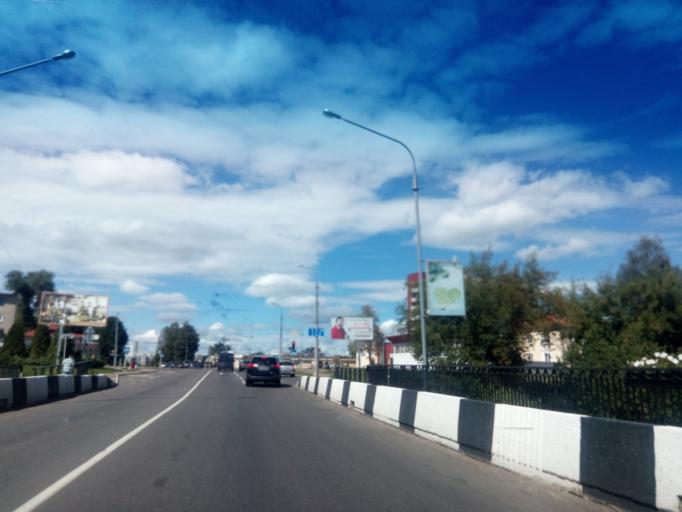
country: BY
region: Vitebsk
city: Polatsk
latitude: 55.4938
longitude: 28.7707
